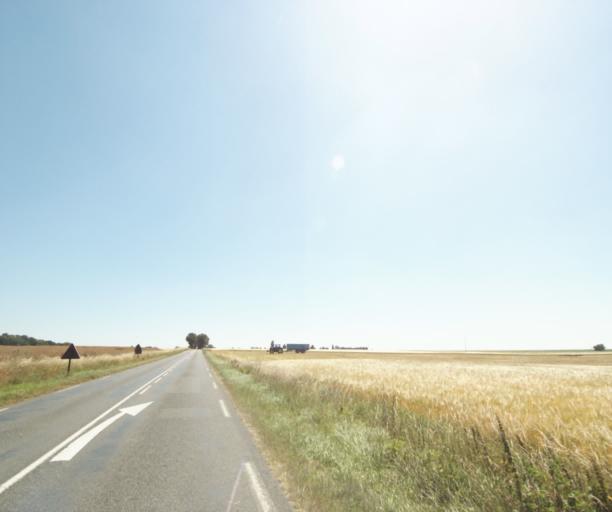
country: FR
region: Ile-de-France
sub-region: Departement de l'Essonne
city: Milly-la-Foret
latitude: 48.3533
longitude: 2.4550
